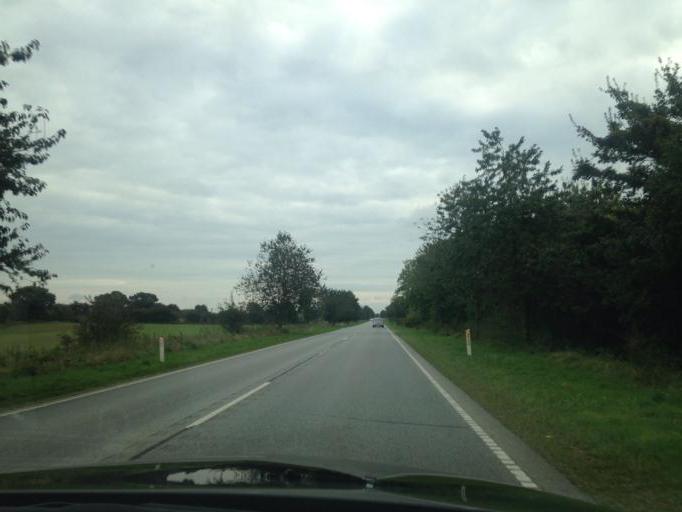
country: DK
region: South Denmark
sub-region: Haderslev Kommune
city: Vojens
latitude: 55.2509
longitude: 9.3641
